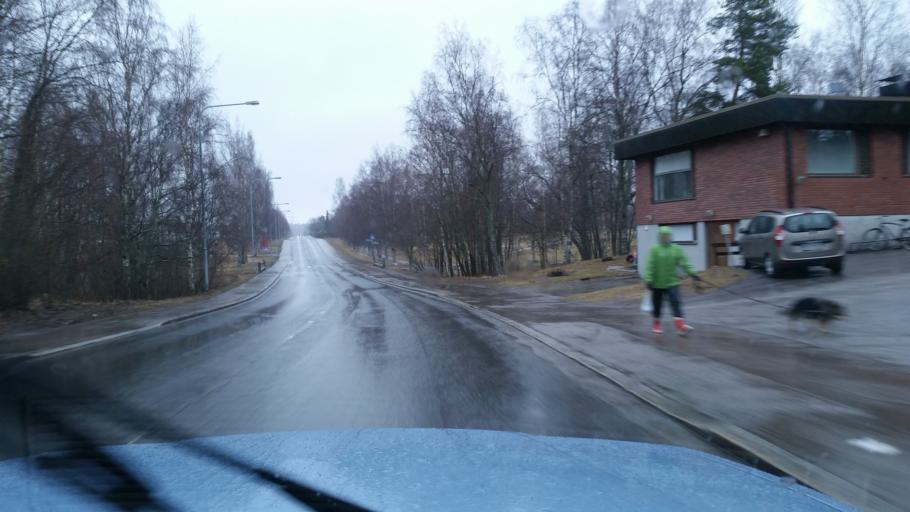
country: FI
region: Pirkanmaa
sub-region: Tampere
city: Tampere
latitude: 61.4735
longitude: 23.7981
